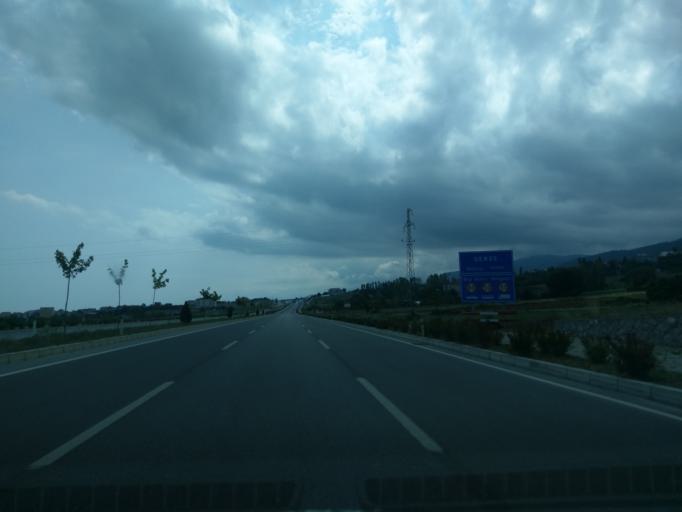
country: TR
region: Sinop
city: Gerze
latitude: 41.8082
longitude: 35.1703
